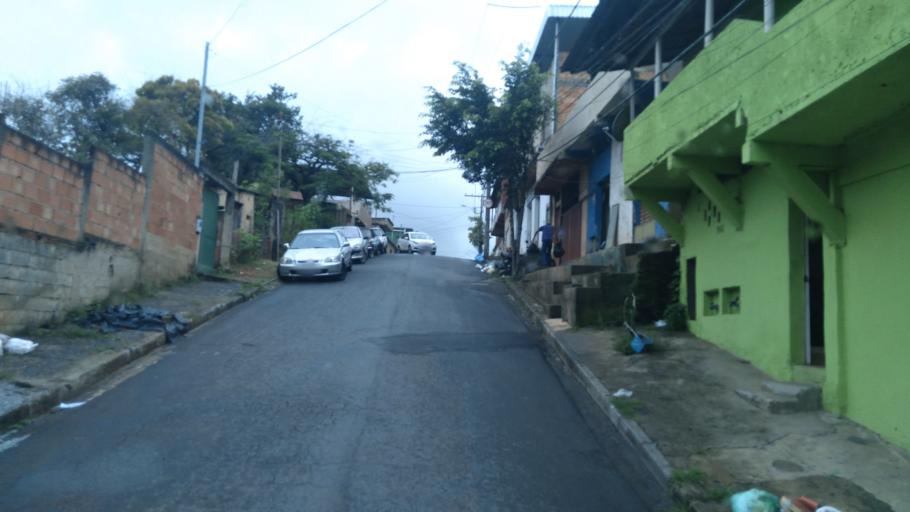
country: BR
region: Minas Gerais
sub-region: Belo Horizonte
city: Belo Horizonte
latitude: -19.9176
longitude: -43.8858
